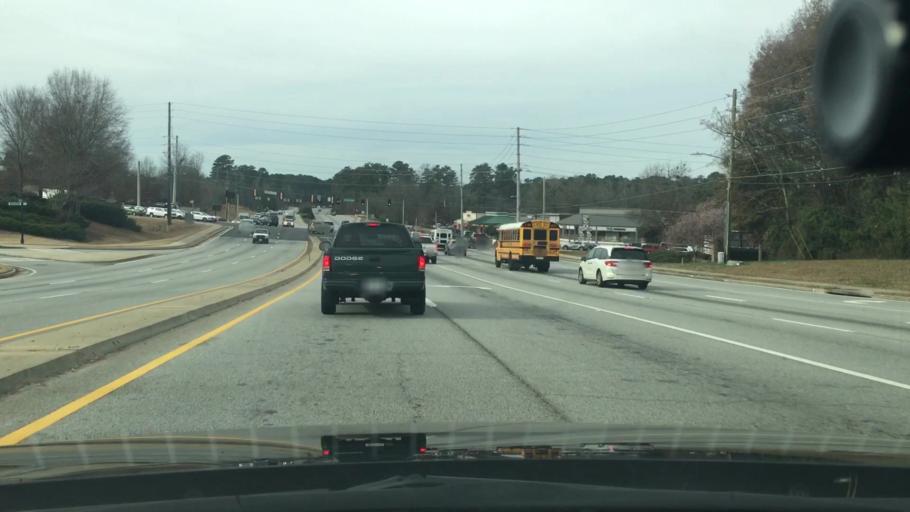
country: US
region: Georgia
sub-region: Fayette County
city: Peachtree City
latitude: 33.3965
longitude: -84.5896
